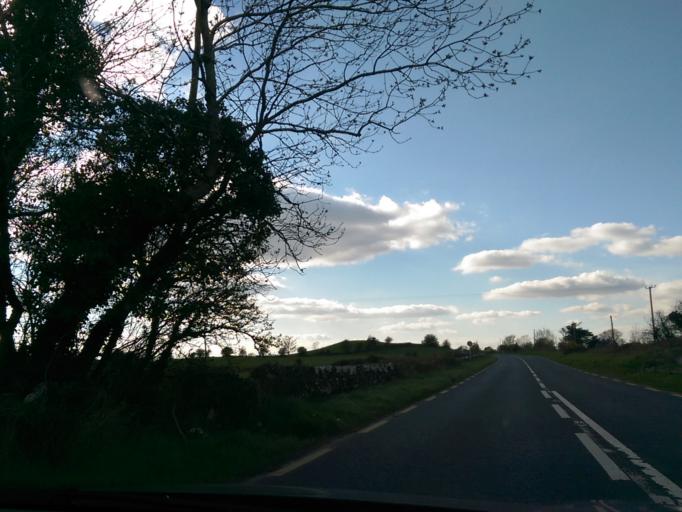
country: IE
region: Connaught
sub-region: County Galway
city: Loughrea
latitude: 53.1923
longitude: -8.3846
